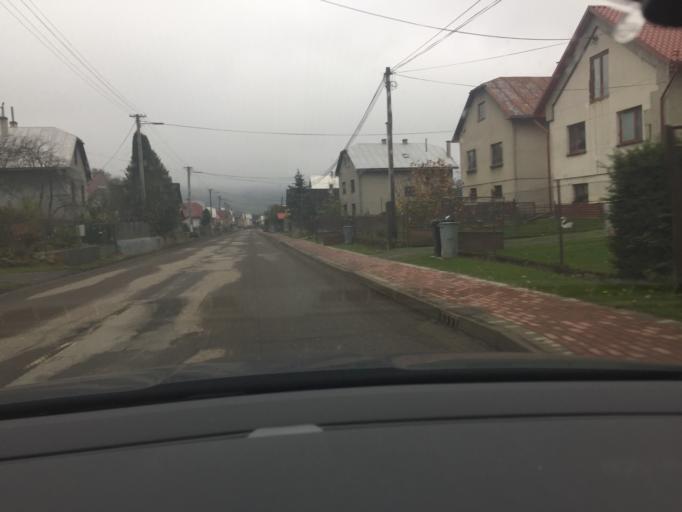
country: PL
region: Lesser Poland Voivodeship
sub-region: Powiat nowosadecki
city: Tylicz
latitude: 49.3070
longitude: 21.0488
